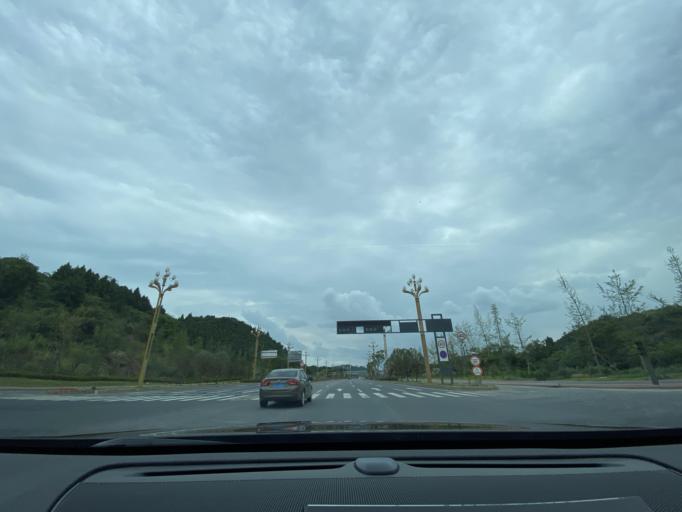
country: CN
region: Sichuan
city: Jiancheng
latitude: 30.4652
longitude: 104.4952
